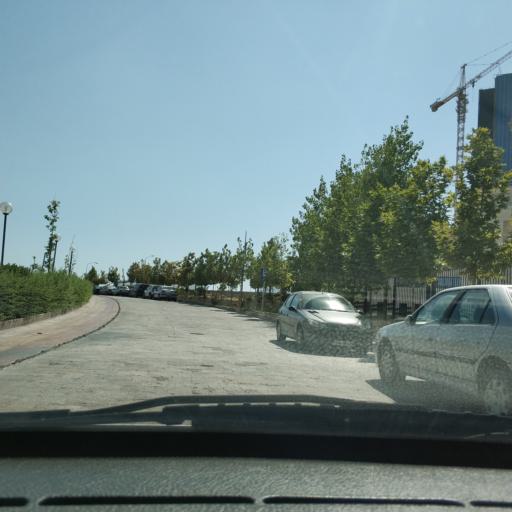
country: IR
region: Tehran
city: Tajrish
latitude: 35.7566
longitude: 51.4315
